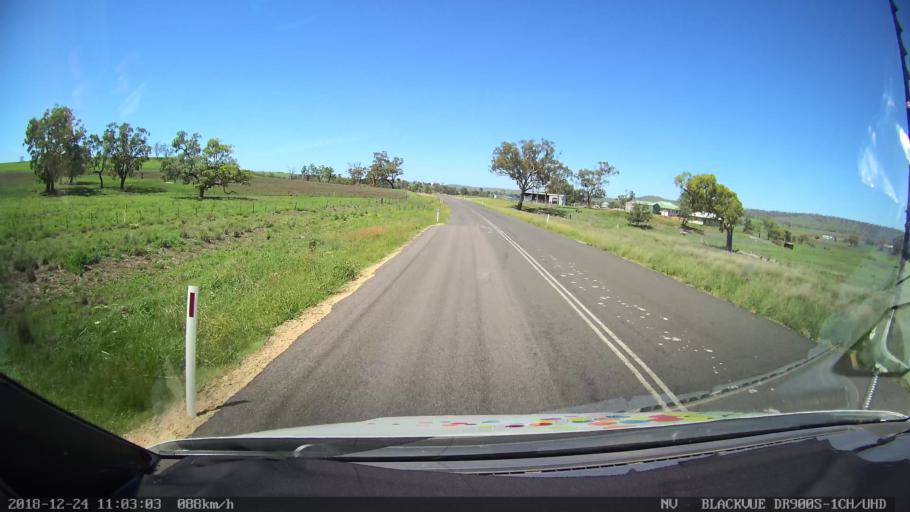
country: AU
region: New South Wales
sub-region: Upper Hunter Shire
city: Merriwa
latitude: -32.0919
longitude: 150.3700
